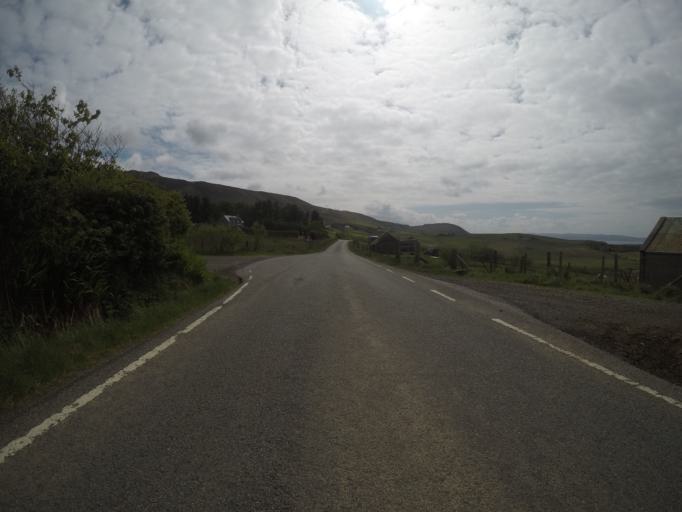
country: GB
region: Scotland
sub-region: Highland
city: Portree
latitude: 57.6181
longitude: -6.3720
